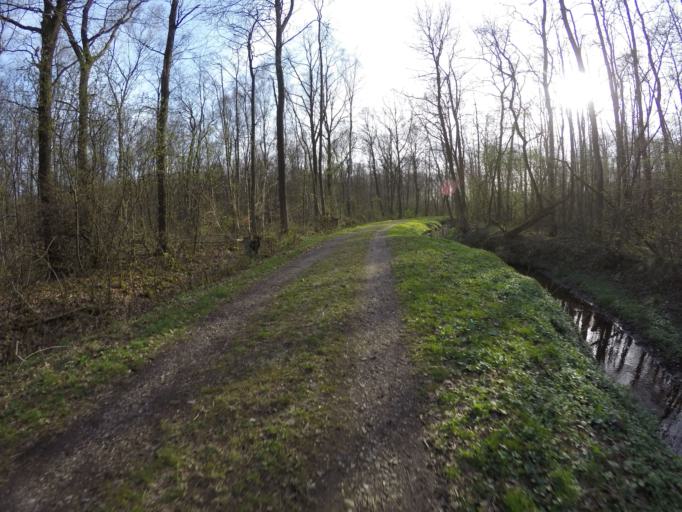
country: DE
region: Schleswig-Holstein
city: Hemdingen
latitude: 53.7417
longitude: 9.8311
